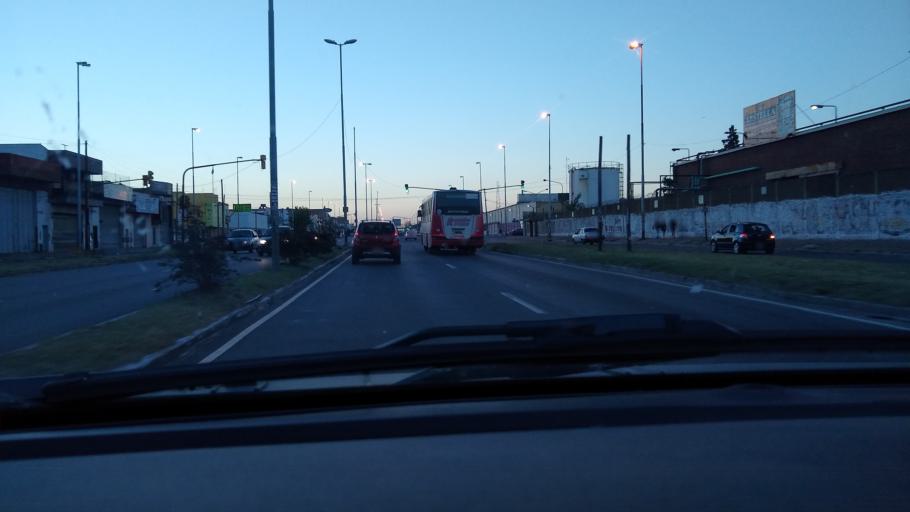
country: AR
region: Buenos Aires
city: San Justo
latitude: -34.6903
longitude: -58.5542
